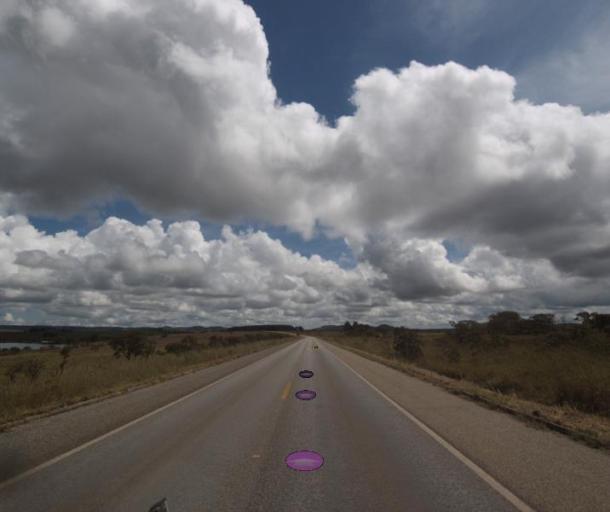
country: BR
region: Goias
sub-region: Pirenopolis
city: Pirenopolis
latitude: -15.7489
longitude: -48.6610
